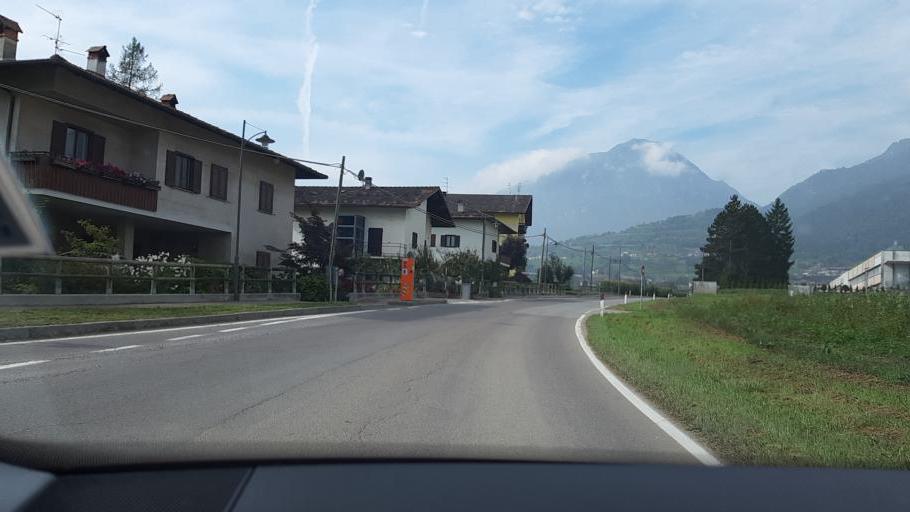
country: IT
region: Trentino-Alto Adige
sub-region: Provincia di Trento
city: Ponte Arche
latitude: 46.0328
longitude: 10.8624
